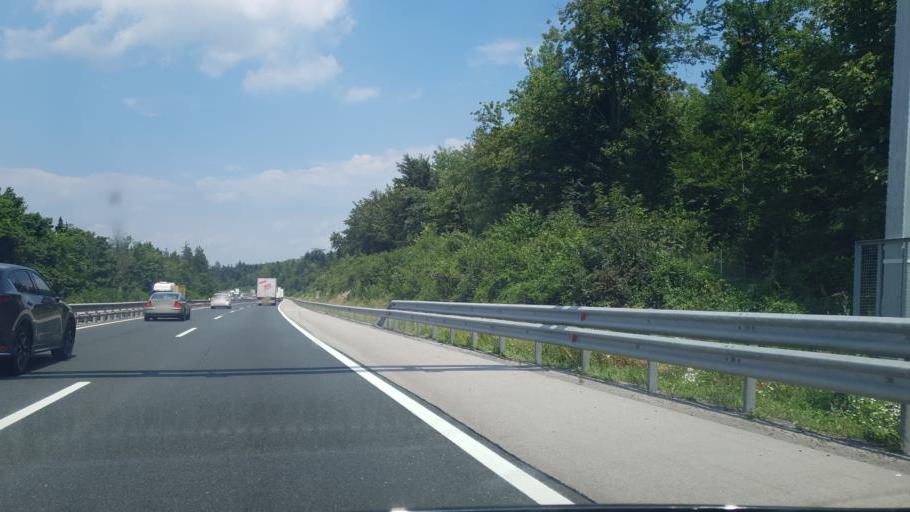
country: SI
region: Cerknica
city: Rakek
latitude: 45.8640
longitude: 14.2717
